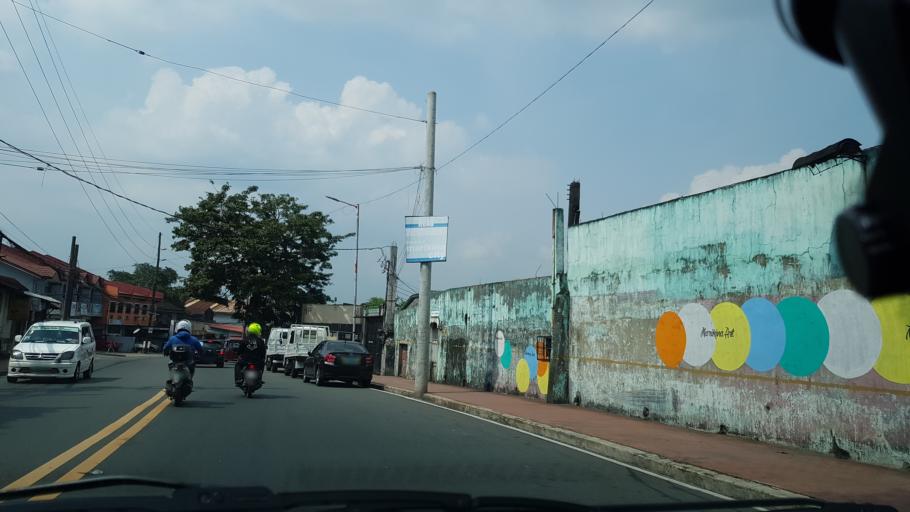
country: PH
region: Calabarzon
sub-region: Province of Rizal
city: Antipolo
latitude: 14.6606
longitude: 121.1187
